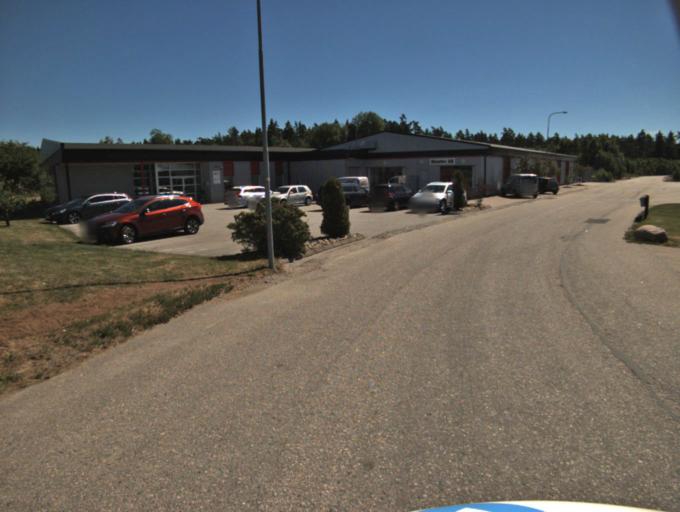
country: SE
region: Vaestra Goetaland
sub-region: Ulricehamns Kommun
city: Ulricehamn
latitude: 57.6713
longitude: 13.4333
